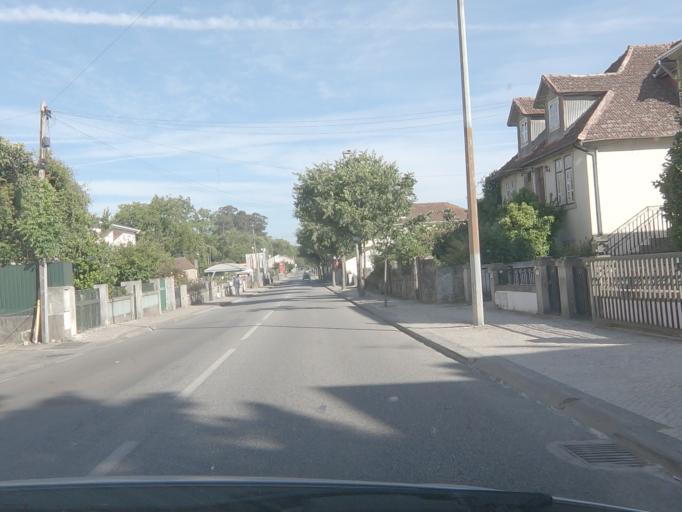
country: PT
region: Viseu
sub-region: Viseu
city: Abraveses
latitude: 40.6702
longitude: -7.9179
